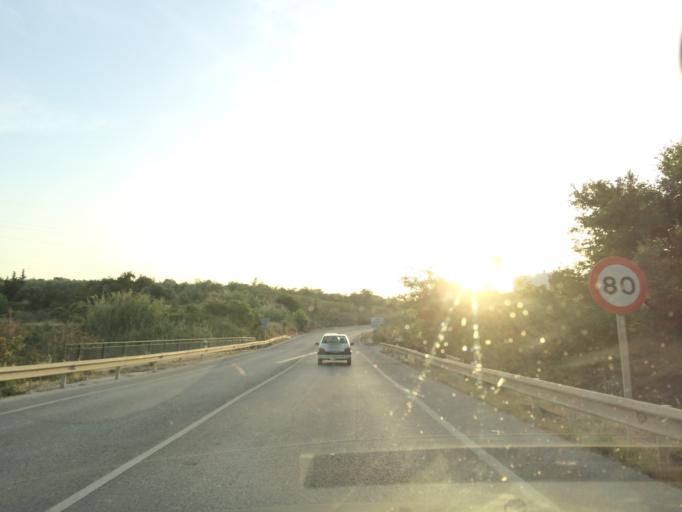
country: ES
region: Andalusia
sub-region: Provincia de Malaga
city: Alhaurin de la Torre
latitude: 36.6711
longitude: -4.5562
